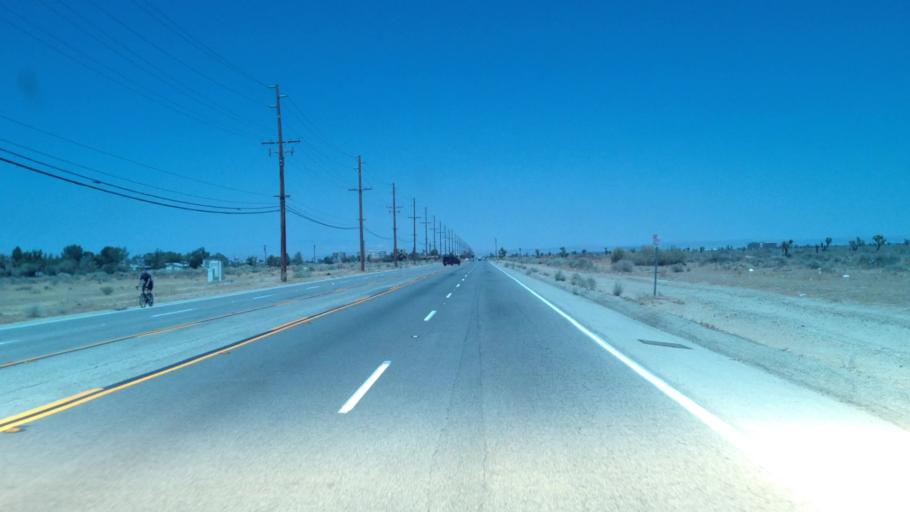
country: US
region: California
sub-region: Los Angeles County
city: Desert View Highlands
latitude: 34.6185
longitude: -118.1477
